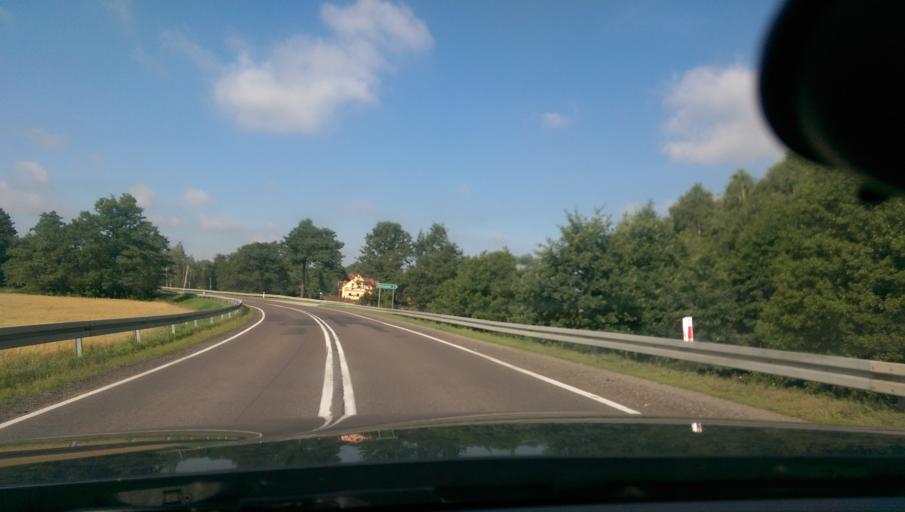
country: PL
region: Masovian Voivodeship
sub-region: Powiat plonski
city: Sochocin
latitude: 52.6850
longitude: 20.4660
